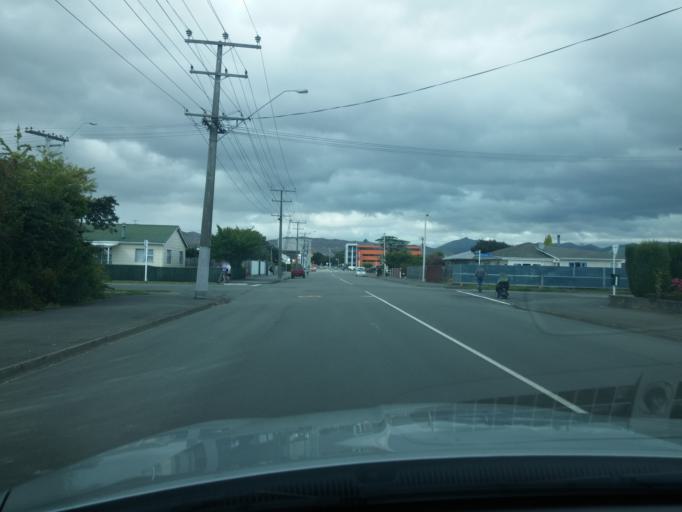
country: NZ
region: Marlborough
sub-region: Marlborough District
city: Blenheim
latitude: -41.5059
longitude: 173.9555
